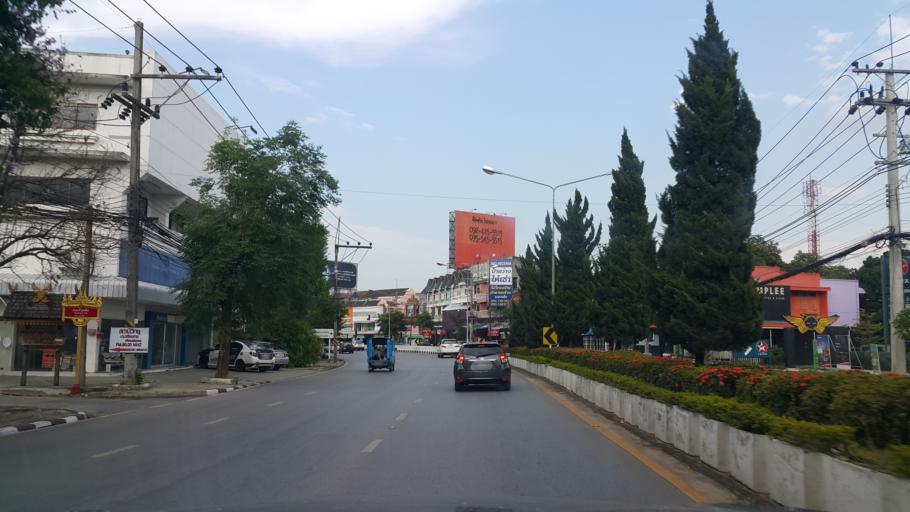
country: TH
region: Chiang Rai
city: Chiang Rai
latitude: 19.9147
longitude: 99.8453
